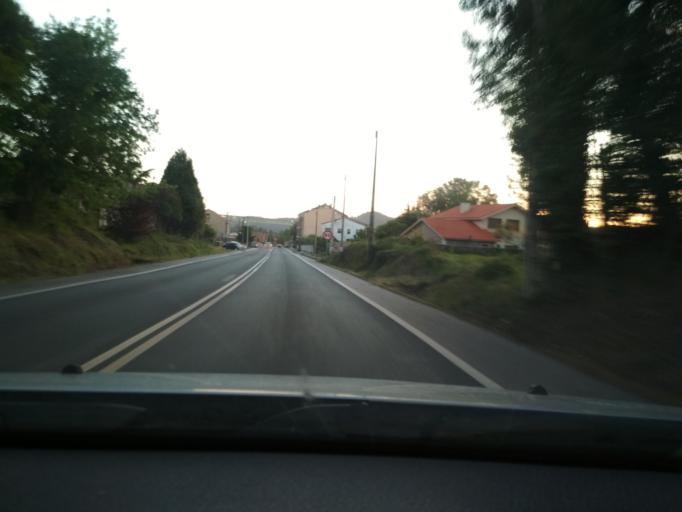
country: ES
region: Galicia
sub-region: Provincia de Pontevedra
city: Catoira
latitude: 42.6695
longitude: -8.7141
